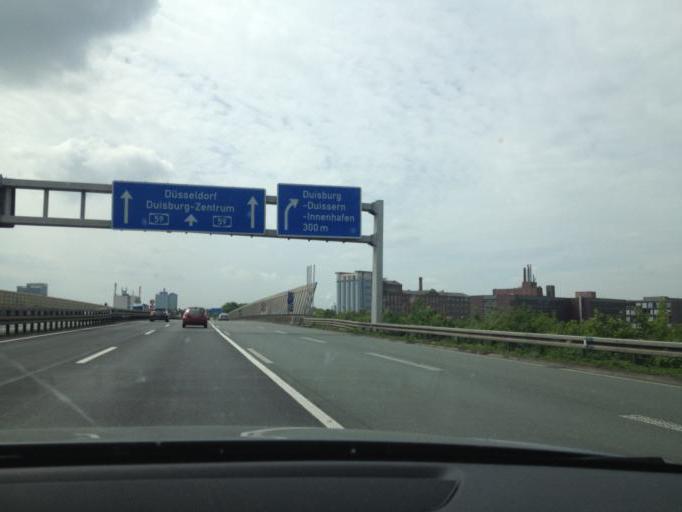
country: DE
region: North Rhine-Westphalia
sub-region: Regierungsbezirk Dusseldorf
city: Duisburg
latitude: 51.4442
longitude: 6.7779
